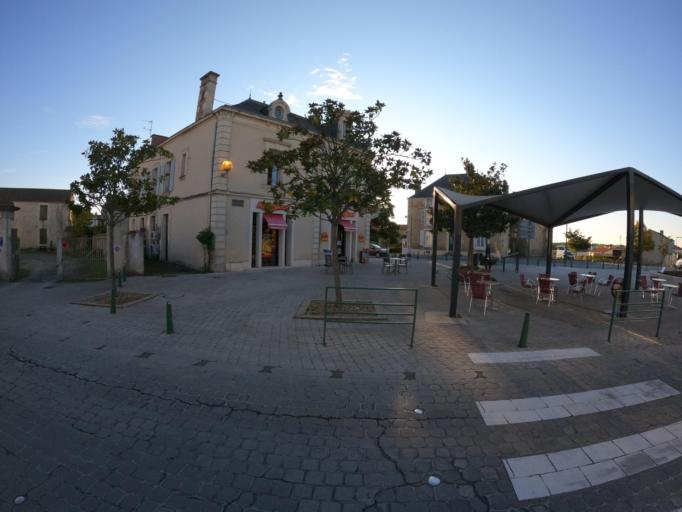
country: FR
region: Pays de la Loire
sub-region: Departement de la Vendee
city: Sainte-Hermine
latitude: 46.5552
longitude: -1.0611
